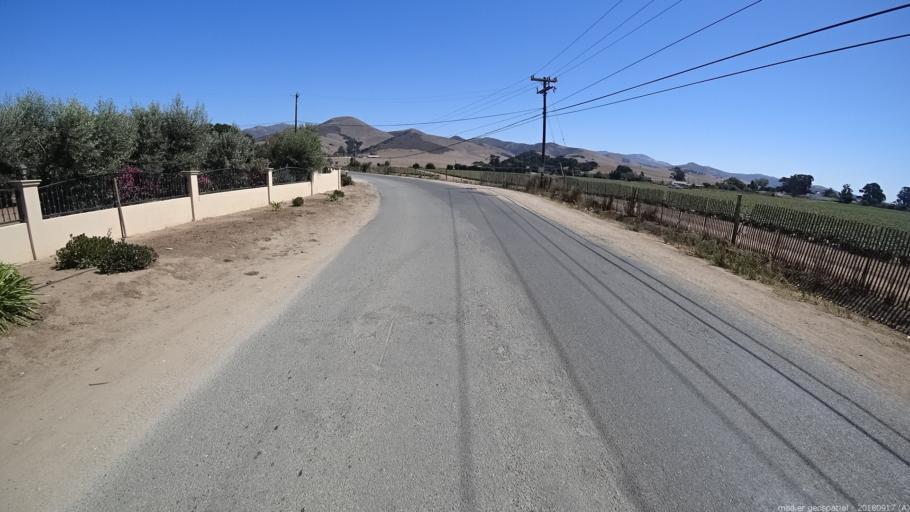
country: US
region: California
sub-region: Monterey County
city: Salinas
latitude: 36.7310
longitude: -121.6014
